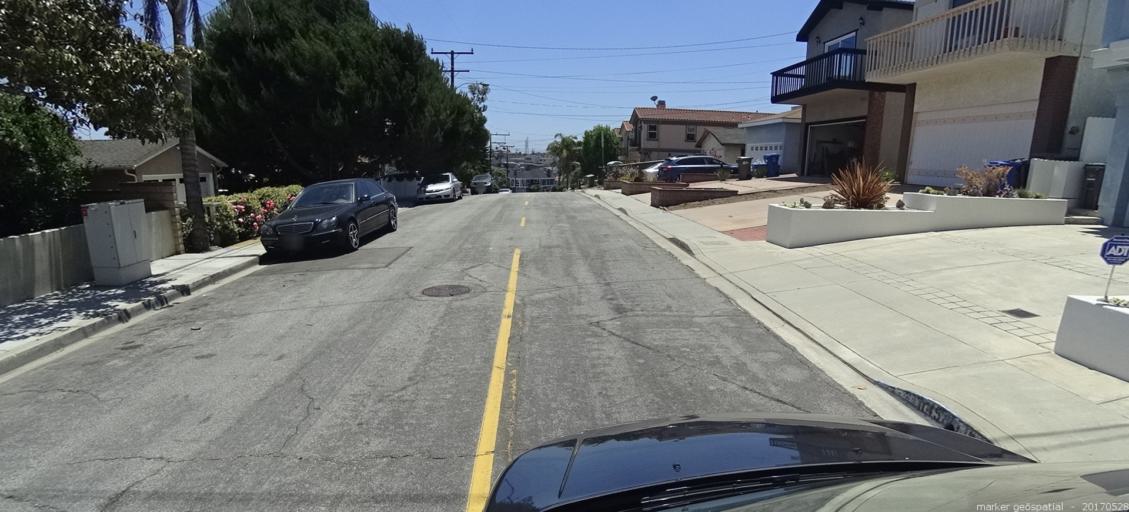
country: US
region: California
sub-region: Los Angeles County
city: Hermosa Beach
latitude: 33.8641
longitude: -118.3848
